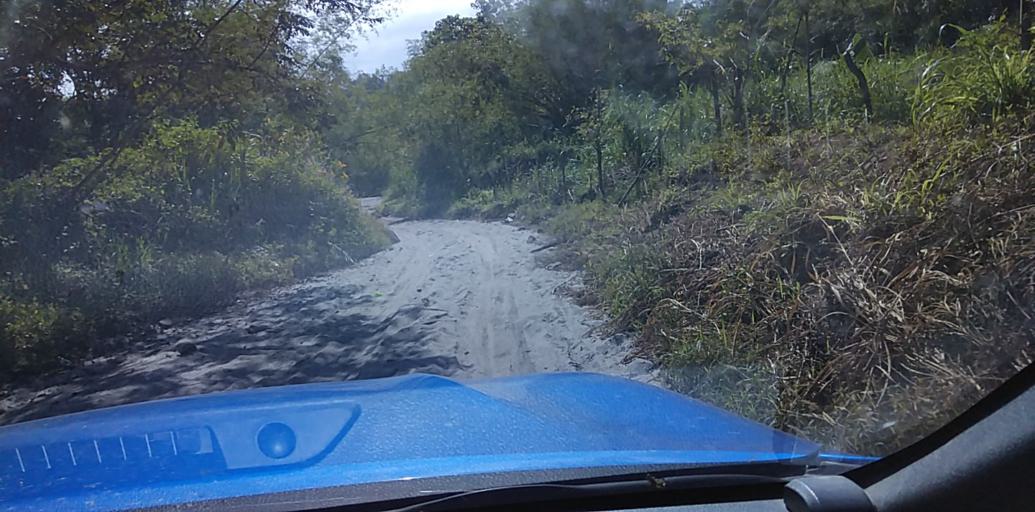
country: PH
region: Central Luzon
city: Santol
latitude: 15.1696
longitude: 120.4812
